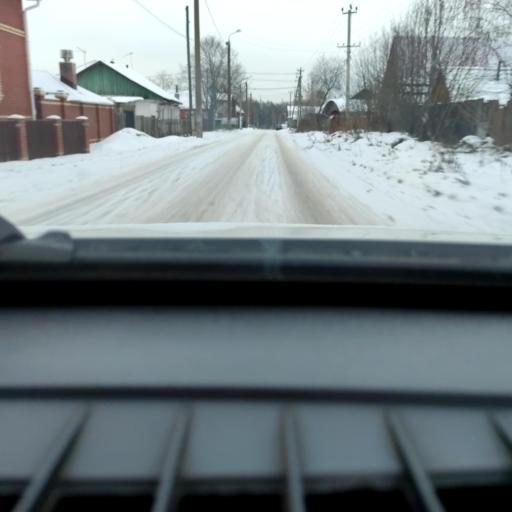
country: RU
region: Perm
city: Perm
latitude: 58.0998
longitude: 56.3682
